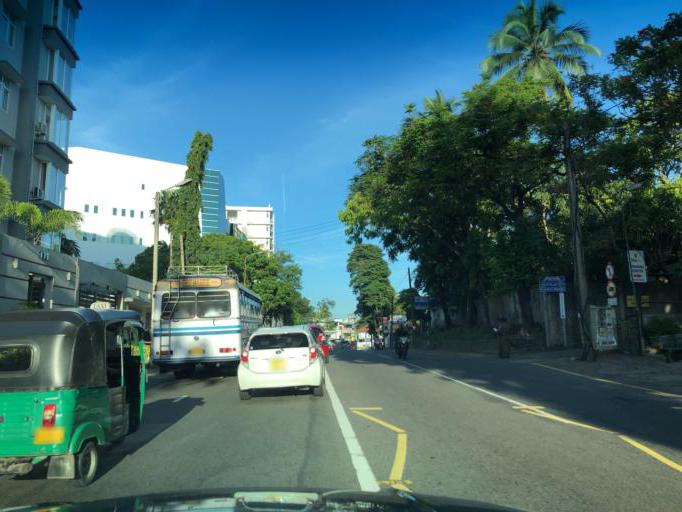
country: LK
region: Western
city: Pita Kotte
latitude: 6.8724
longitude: 79.8836
